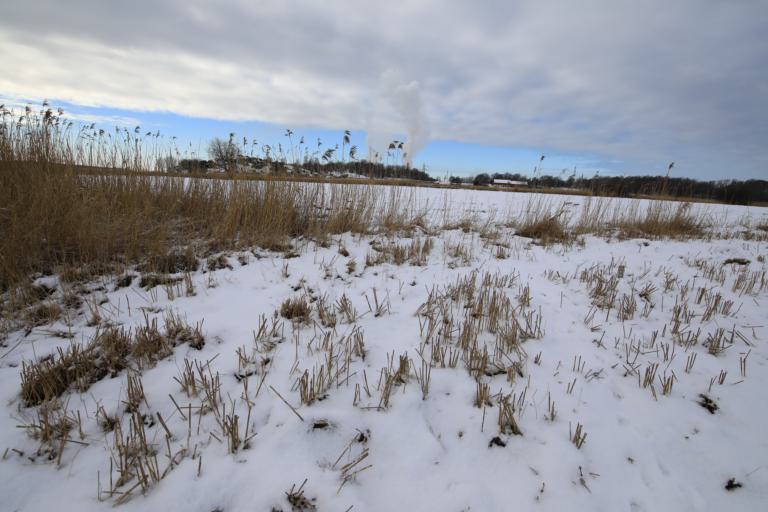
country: SE
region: Halland
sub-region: Kungsbacka Kommun
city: Frillesas
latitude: 57.2276
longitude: 12.2062
